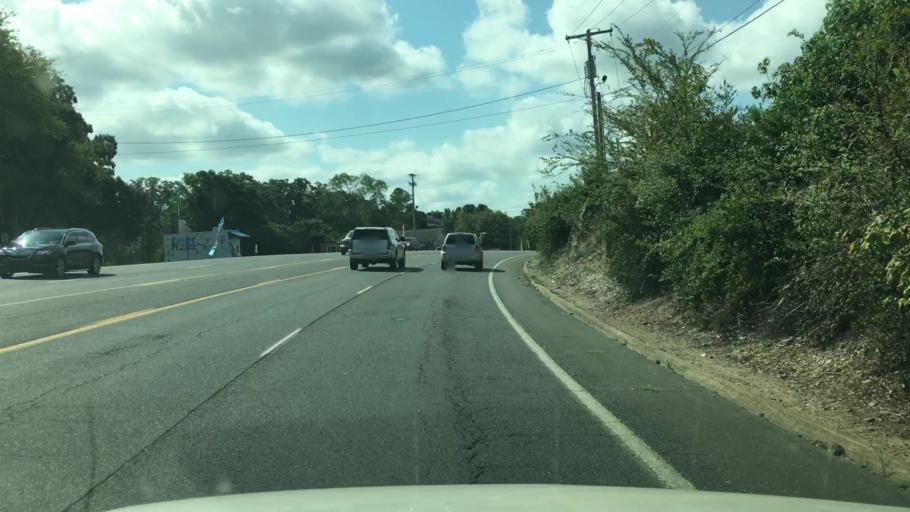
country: US
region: Arkansas
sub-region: Garland County
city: Piney
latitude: 34.5004
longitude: -93.1228
